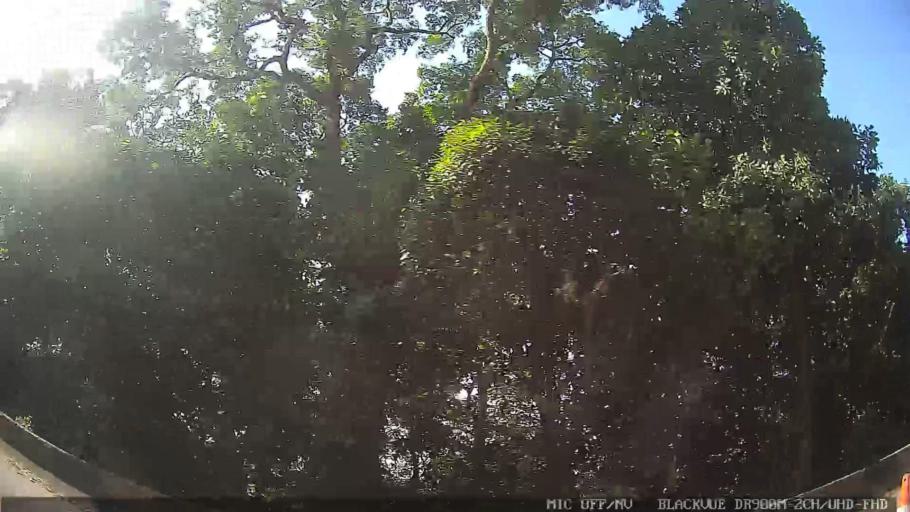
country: BR
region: Sao Paulo
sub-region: Cubatao
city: Cubatao
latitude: -23.8914
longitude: -46.4690
